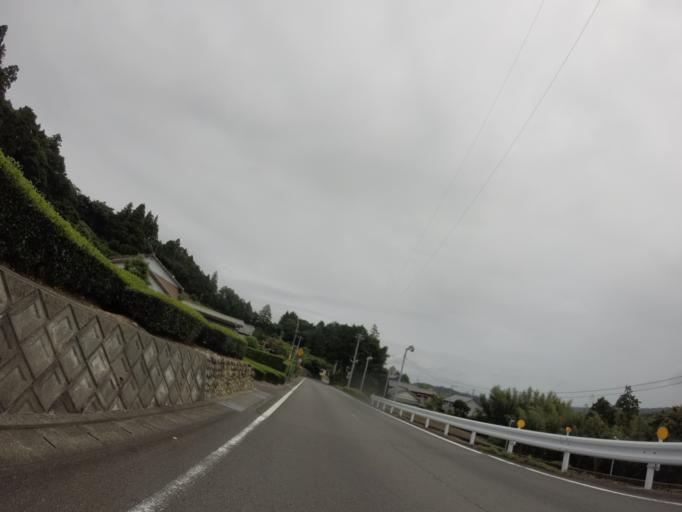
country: JP
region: Shizuoka
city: Kanaya
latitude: 34.7977
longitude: 138.1413
